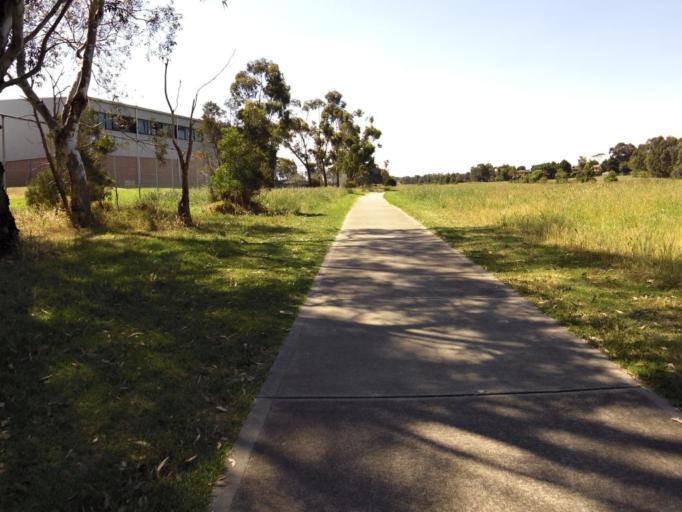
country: AU
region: Victoria
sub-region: Casey
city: Narre Warren South
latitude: -38.0439
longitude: 145.2761
